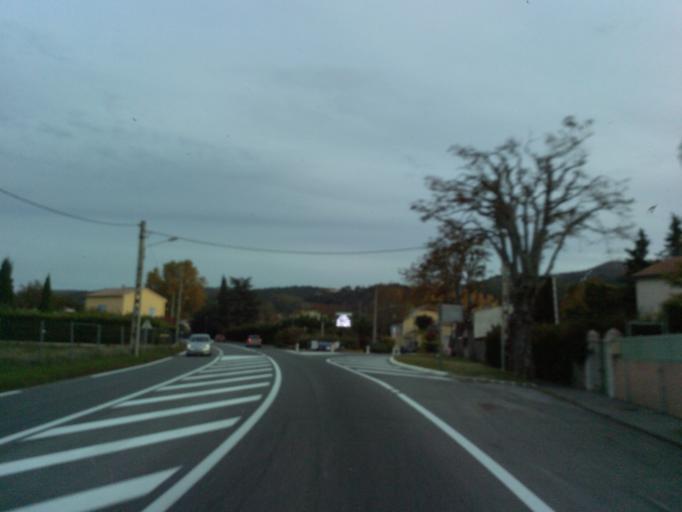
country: FR
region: Provence-Alpes-Cote d'Azur
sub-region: Departement des Alpes-de-Haute-Provence
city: Malijai
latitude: 44.0479
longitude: 6.0262
